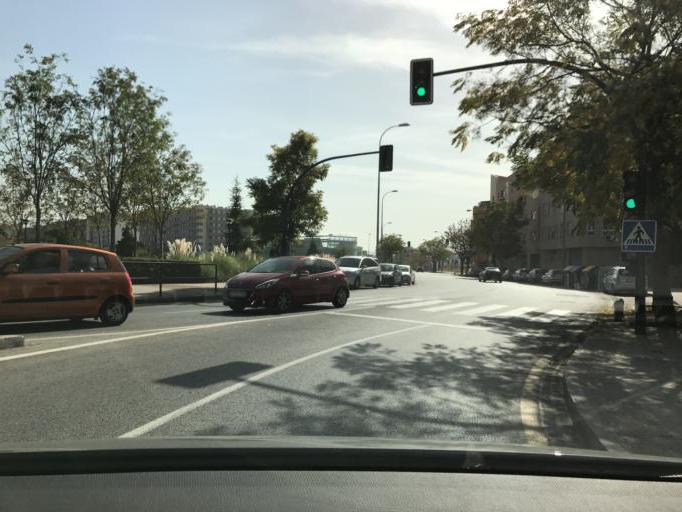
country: ES
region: Andalusia
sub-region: Provincia de Granada
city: Maracena
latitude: 37.2062
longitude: -3.6197
